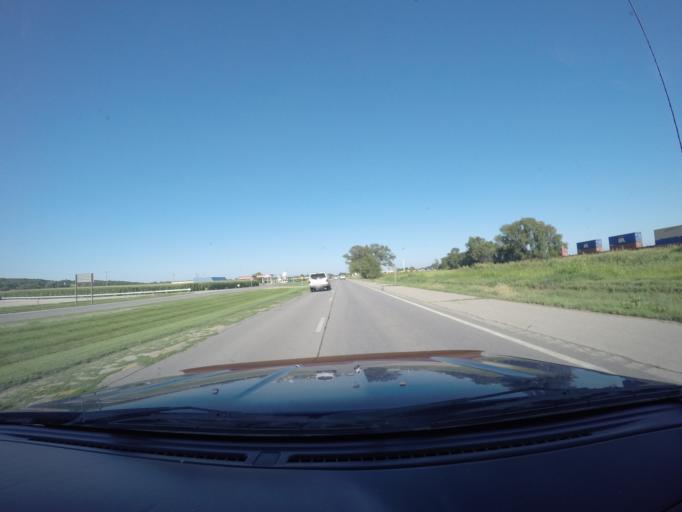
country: US
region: Kansas
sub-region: Shawnee County
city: Topeka
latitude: 39.0877
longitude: -95.5755
